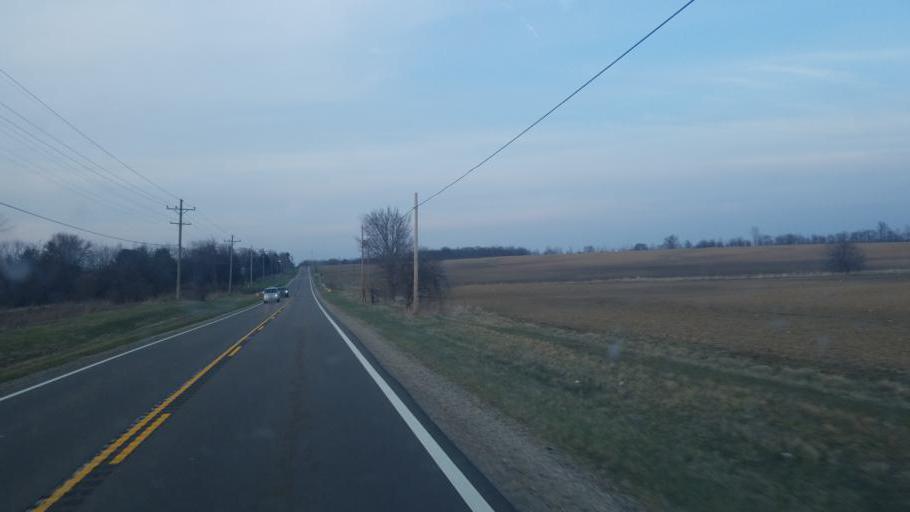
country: US
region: Ohio
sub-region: Marion County
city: Marion
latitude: 40.5236
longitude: -83.1646
